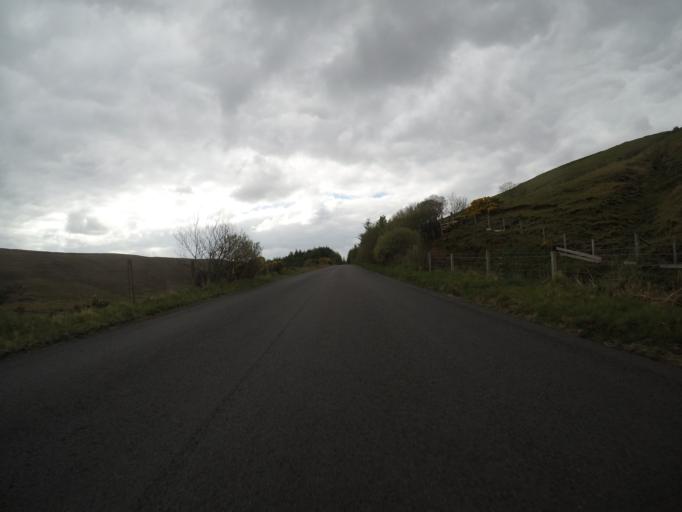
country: GB
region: Scotland
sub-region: Highland
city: Isle of Skye
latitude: 57.2970
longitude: -6.2821
